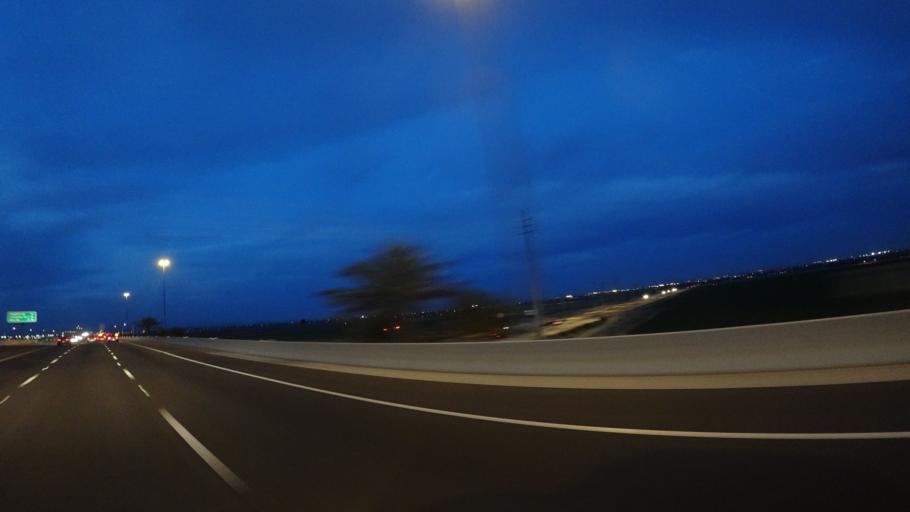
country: US
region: Arizona
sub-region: Maricopa County
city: Citrus Park
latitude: 33.5946
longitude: -112.4180
